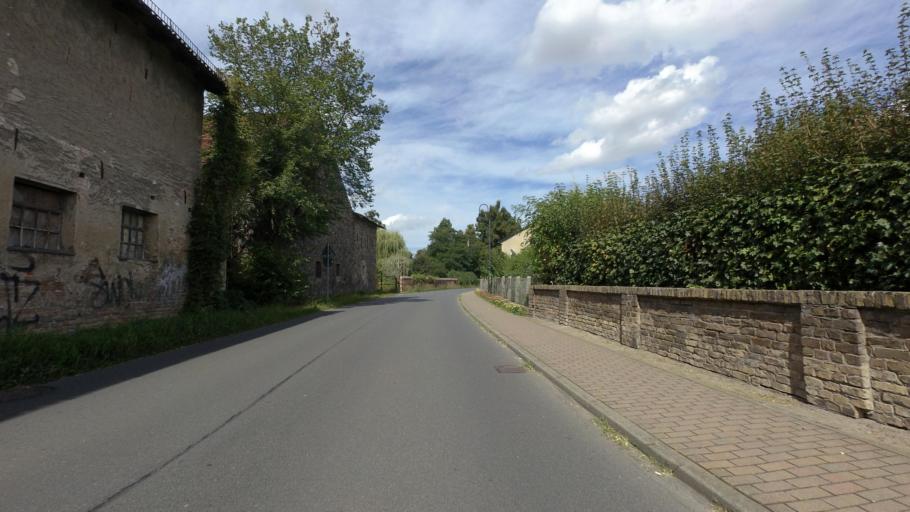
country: DE
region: Brandenburg
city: Gross Kreutz
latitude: 52.4061
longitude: 12.7764
